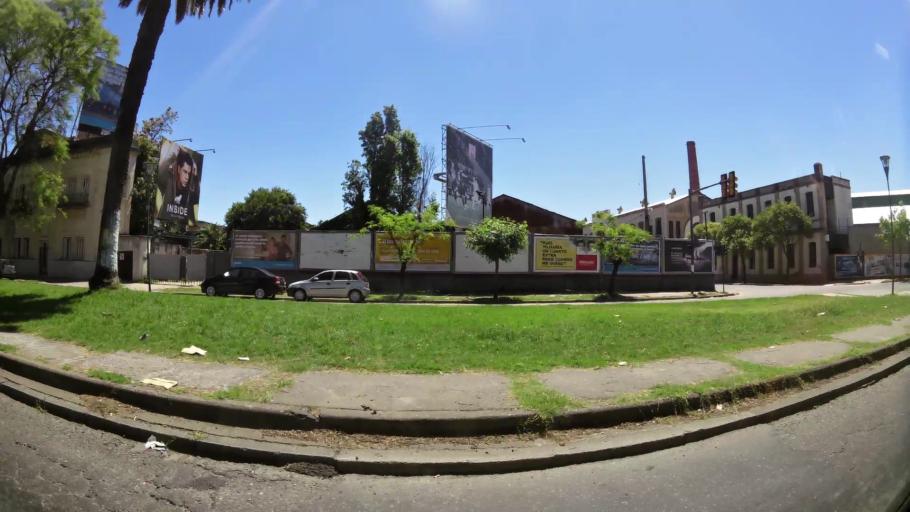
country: AR
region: Santa Fe
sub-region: Departamento de Rosario
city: Rosario
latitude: -32.9325
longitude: -60.6632
